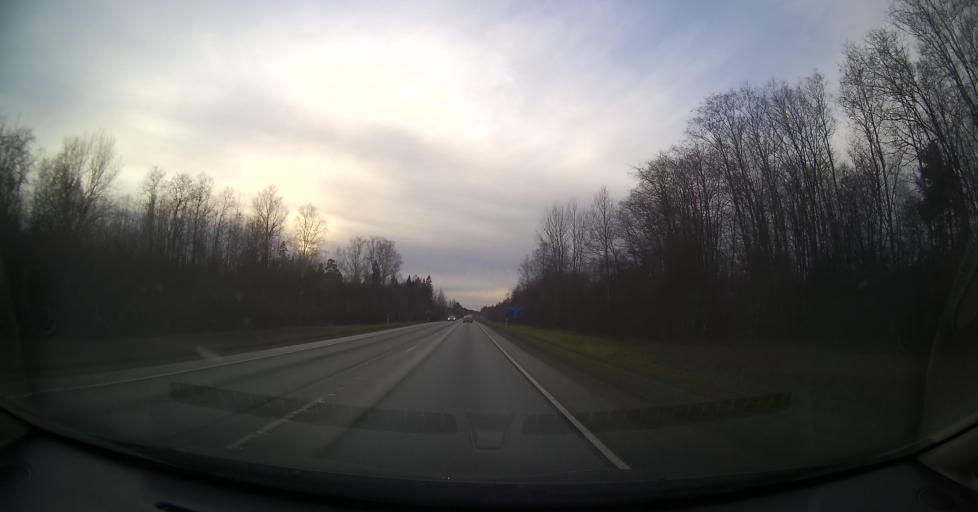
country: EE
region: Ida-Virumaa
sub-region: Johvi vald
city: Johvi
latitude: 59.3667
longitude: 27.4760
